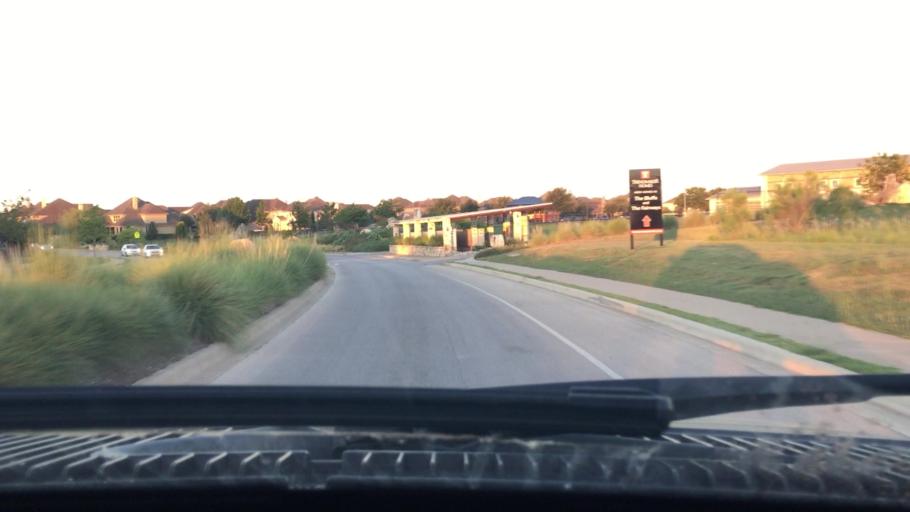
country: US
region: Texas
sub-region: Williamson County
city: Leander
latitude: 30.5376
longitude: -97.8634
